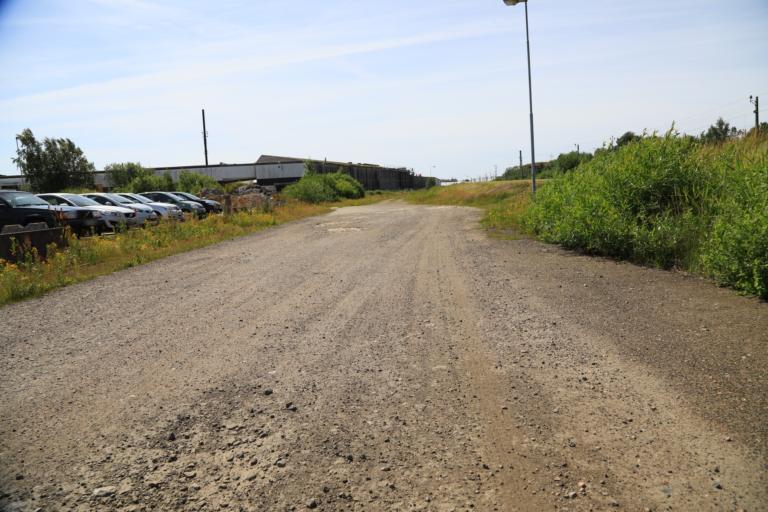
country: SE
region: Halland
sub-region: Varbergs Kommun
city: Varberg
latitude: 57.1199
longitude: 12.2548
